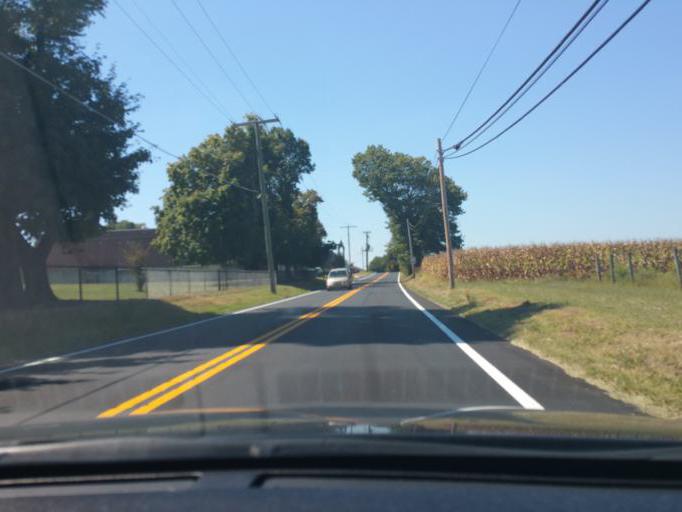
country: US
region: Maryland
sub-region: Harford County
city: Riverside
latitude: 39.5622
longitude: -76.2437
